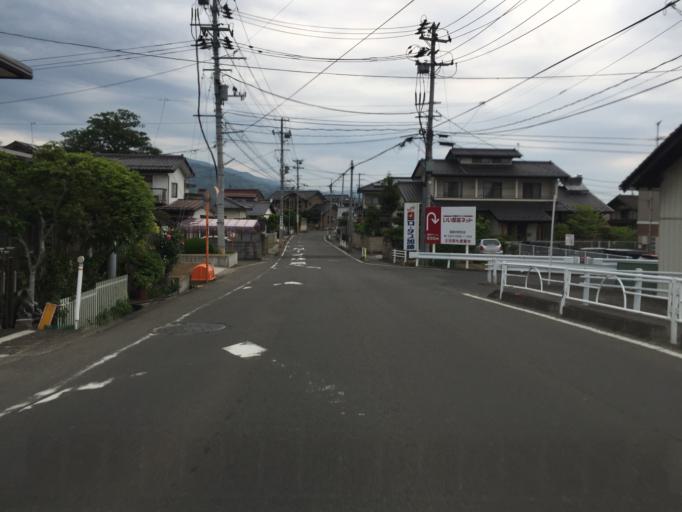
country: JP
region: Fukushima
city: Hobaramachi
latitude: 37.8116
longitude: 140.4955
